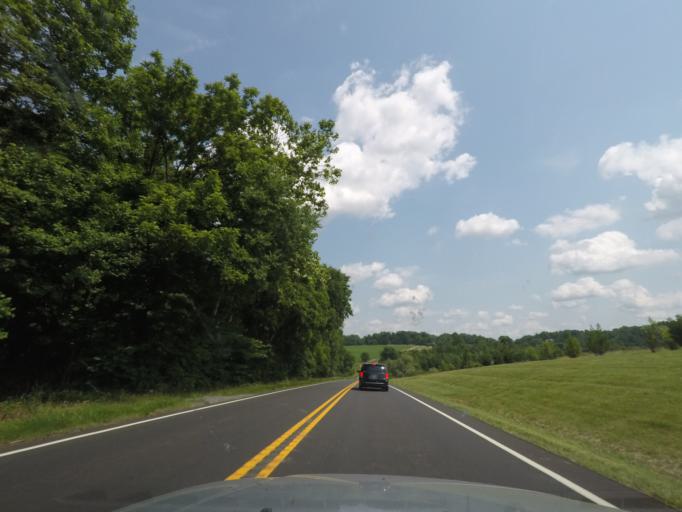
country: US
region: Virginia
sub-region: Orange County
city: Orange
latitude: 38.2752
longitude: -78.1317
